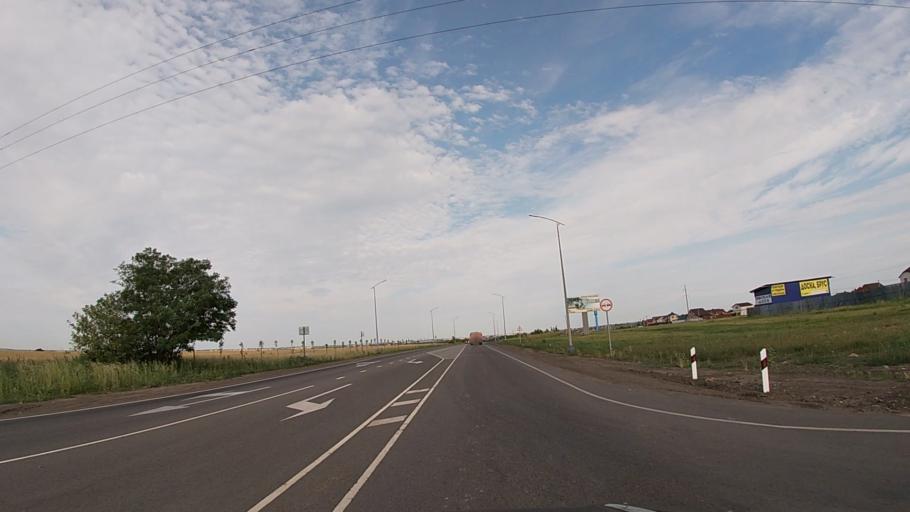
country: RU
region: Belgorod
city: Severnyy
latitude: 50.6651
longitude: 36.5032
